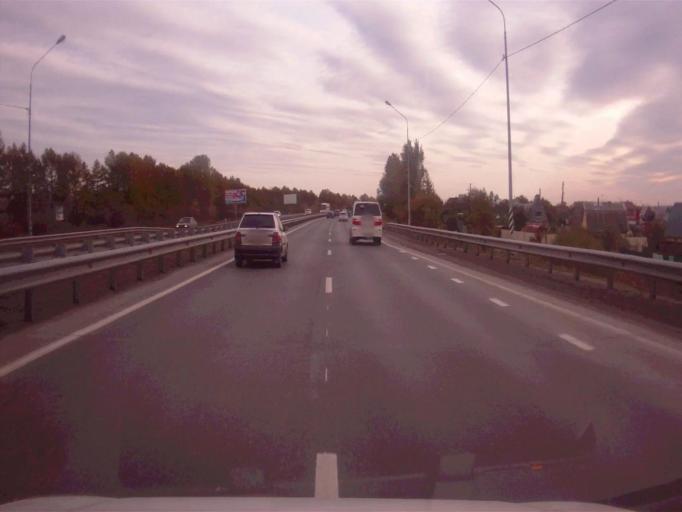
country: RU
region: Chelyabinsk
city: Novosineglazovskiy
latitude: 55.0294
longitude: 61.4477
